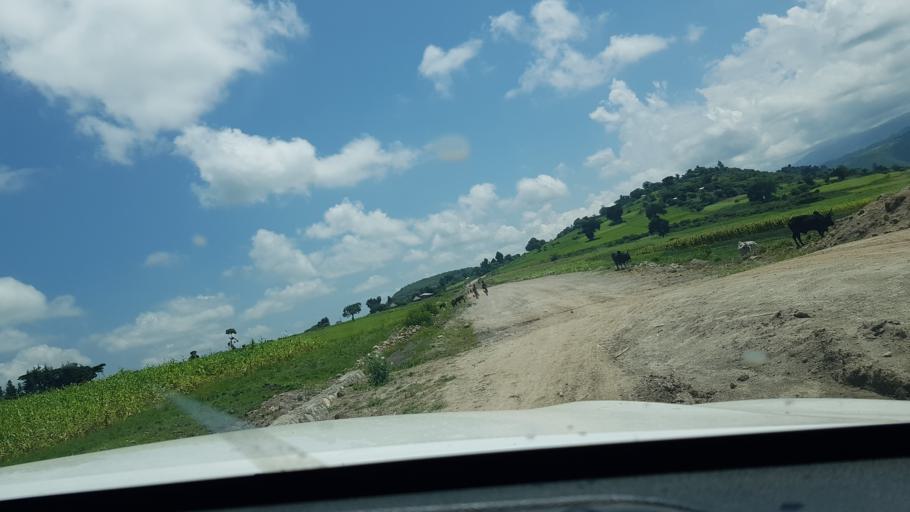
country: ET
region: Oromiya
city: Sirre
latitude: 8.4376
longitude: 39.8779
